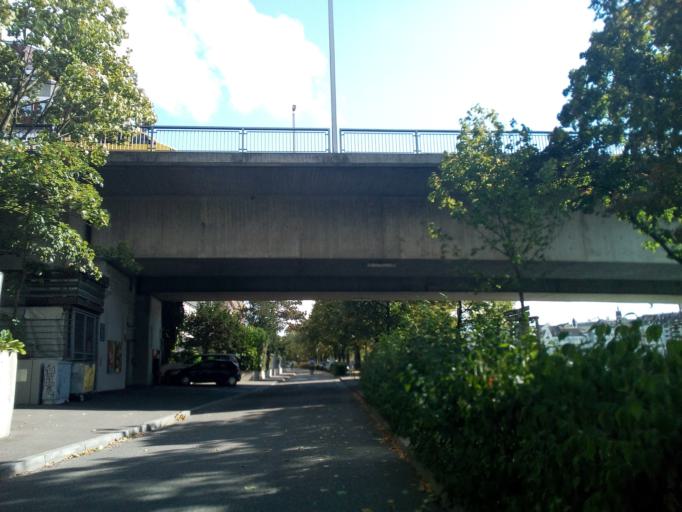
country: CH
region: Basel-City
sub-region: Basel-Stadt
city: Basel
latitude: 47.5657
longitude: 7.5872
